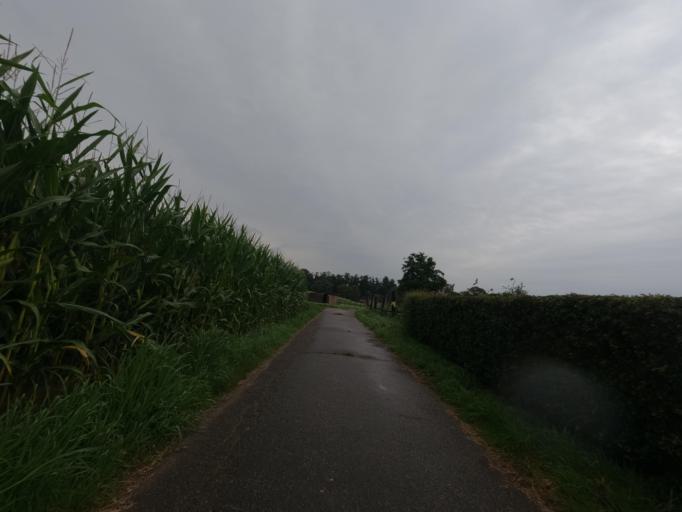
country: DE
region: North Rhine-Westphalia
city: Huckelhoven
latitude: 50.9980
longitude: 6.1883
